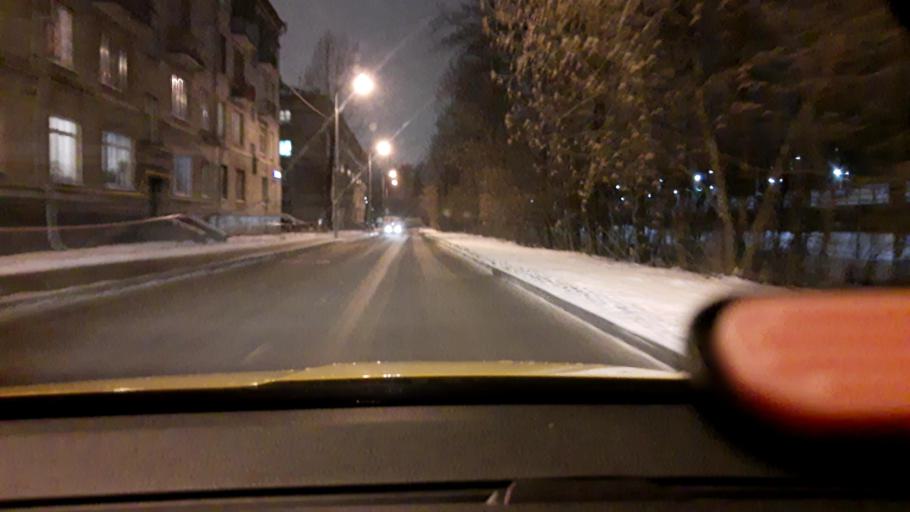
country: RU
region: Moscow
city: Mikhalkovo
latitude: 55.6653
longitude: 37.4210
